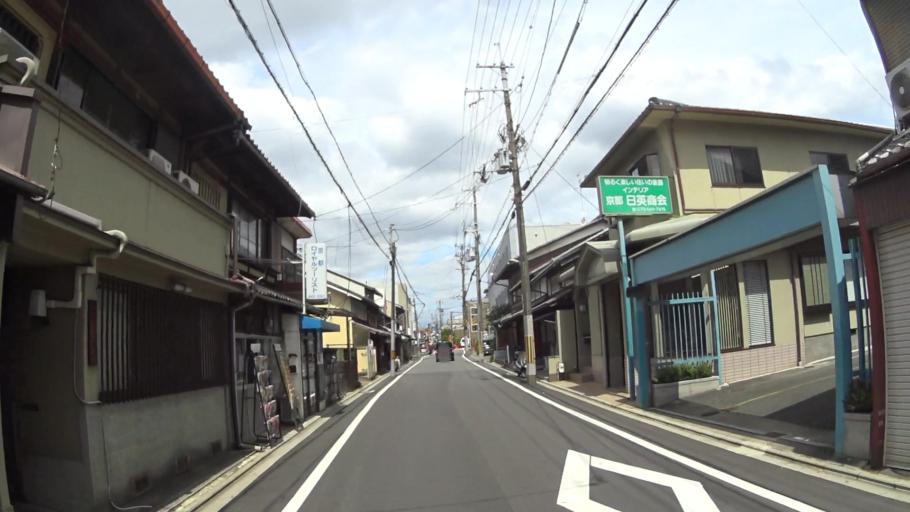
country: JP
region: Kyoto
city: Kyoto
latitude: 34.9649
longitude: 135.7711
